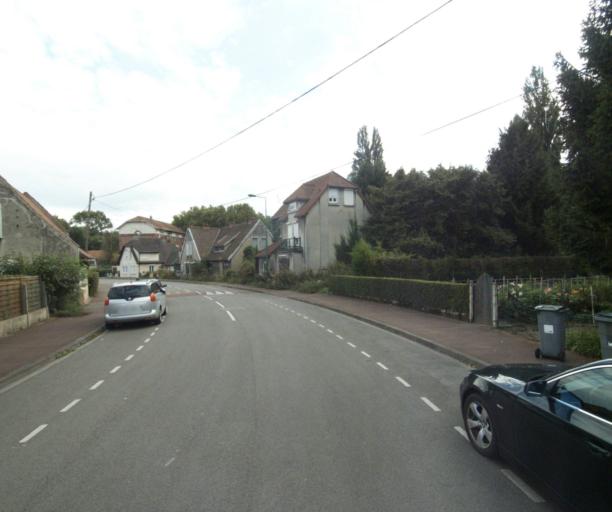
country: FR
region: Nord-Pas-de-Calais
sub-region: Departement du Nord
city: Lomme
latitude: 50.6354
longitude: 2.9886
